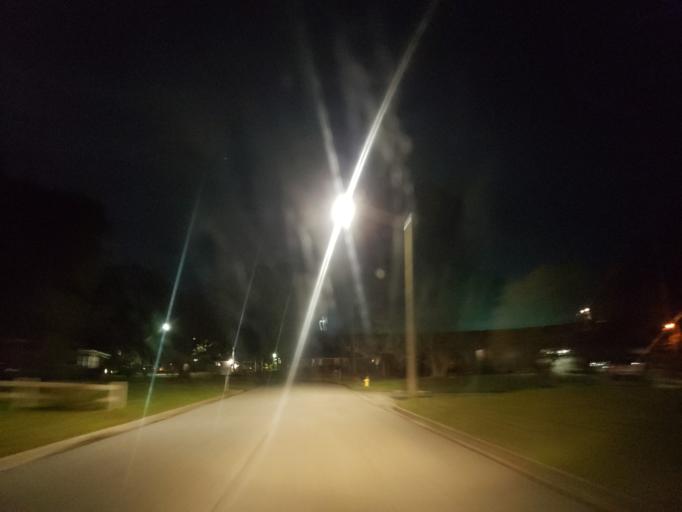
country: US
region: Georgia
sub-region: Chatham County
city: Montgomery
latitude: 31.9874
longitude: -81.1500
